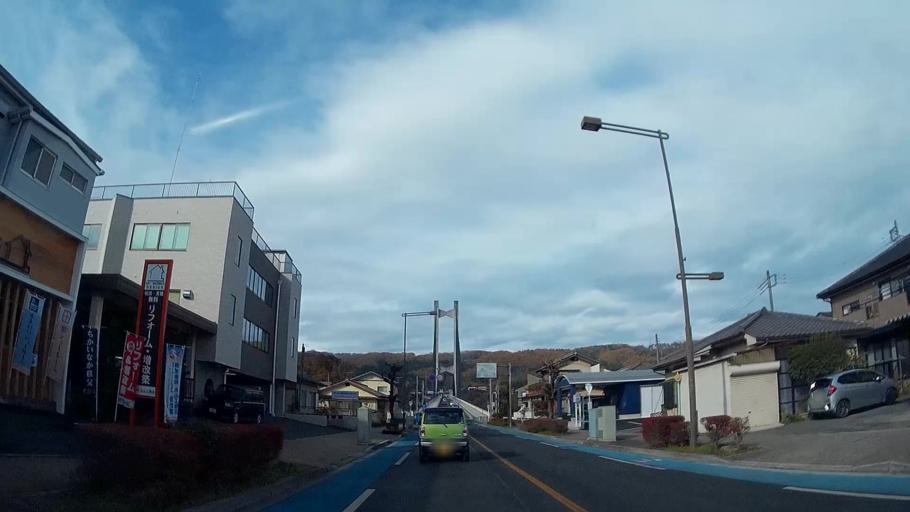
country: JP
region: Saitama
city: Chichibu
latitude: 36.0014
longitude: 139.0766
